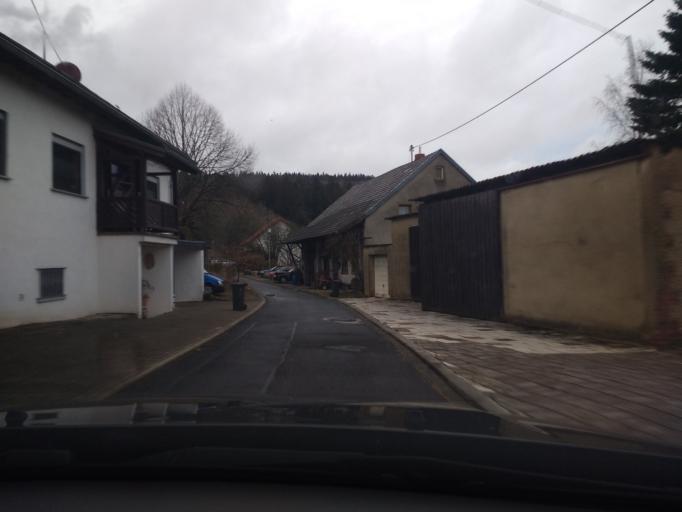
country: DE
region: Rheinland-Pfalz
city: Borfink
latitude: 49.6769
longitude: 7.0491
